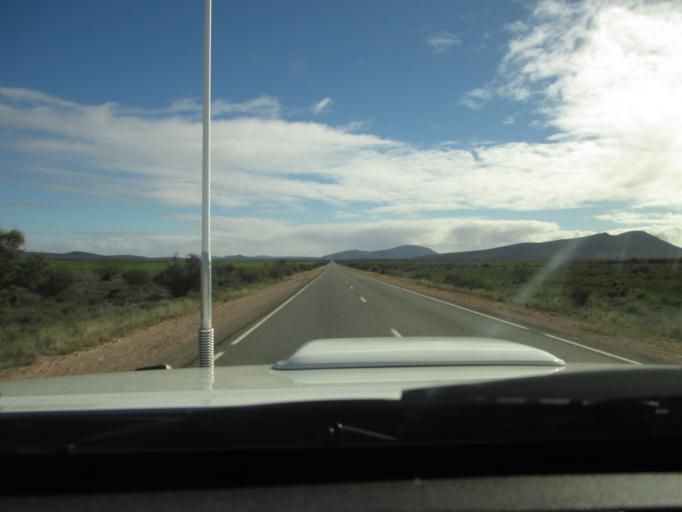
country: AU
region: South Australia
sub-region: Flinders Ranges
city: Quorn
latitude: -31.8739
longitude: 138.4104
